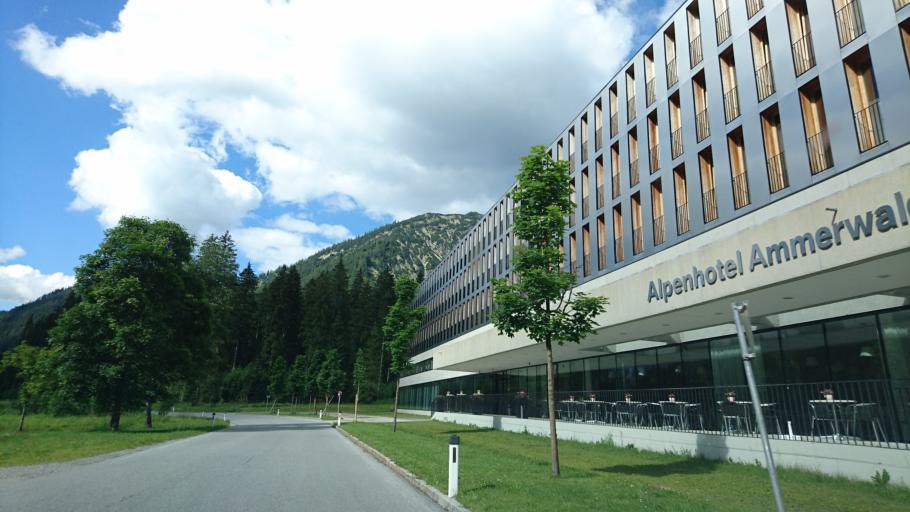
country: DE
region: Bavaria
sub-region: Swabia
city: Halblech
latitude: 47.5253
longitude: 10.8442
